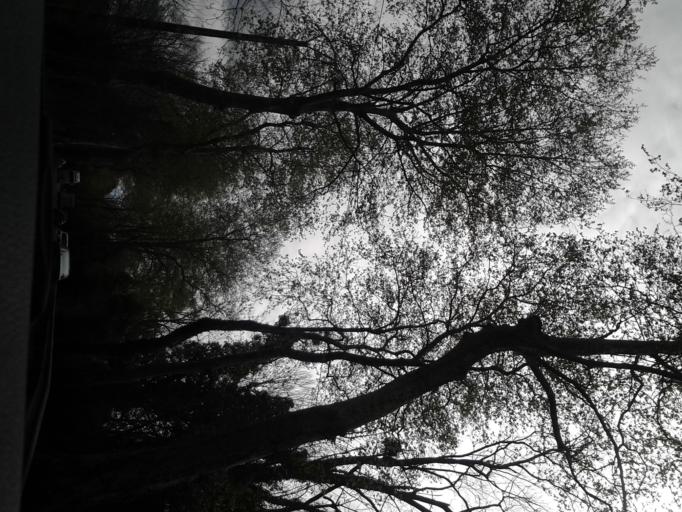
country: FR
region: Aquitaine
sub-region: Departement des Pyrenees-Atlantiques
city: Hendaye
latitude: 43.3498
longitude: -1.7457
